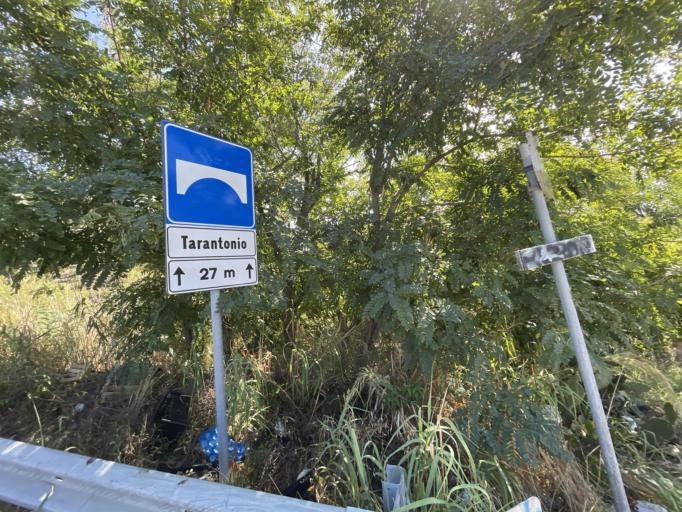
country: IT
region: Sicily
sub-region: Messina
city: Villafranca Tirrena
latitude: 38.2600
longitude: 15.4667
